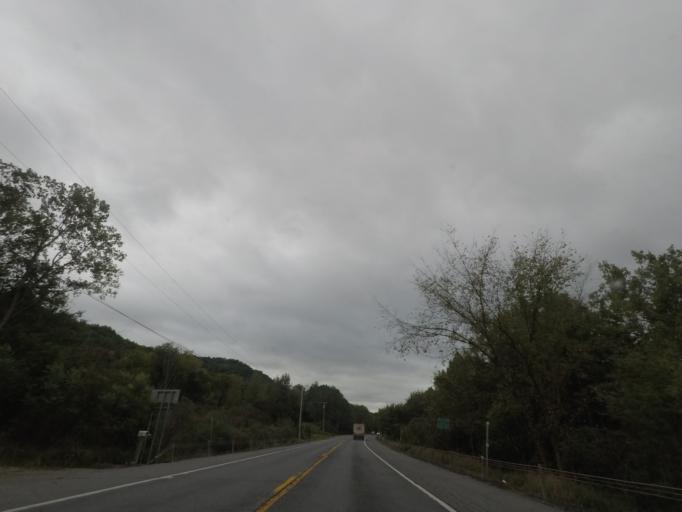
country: US
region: New York
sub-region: Rensselaer County
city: Hoosick Falls
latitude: 42.9437
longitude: -73.3679
